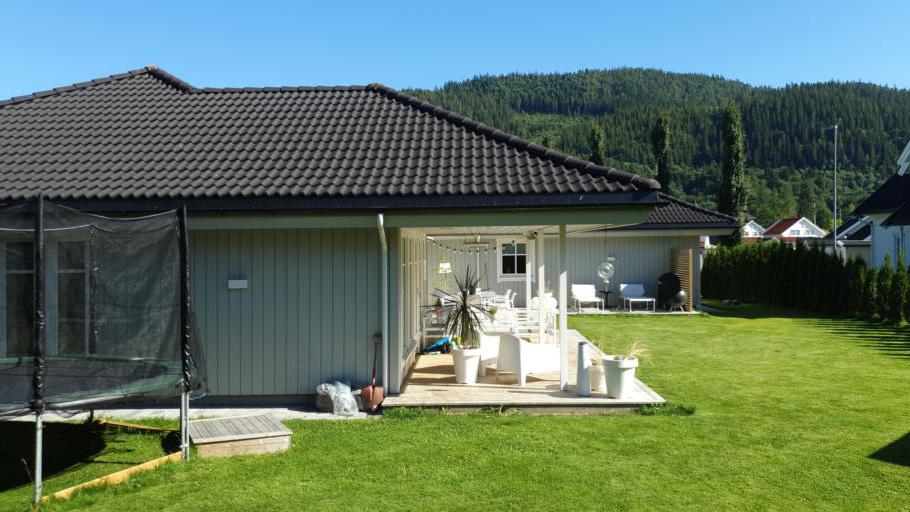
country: NO
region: Sor-Trondelag
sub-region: Orkdal
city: Orkanger
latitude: 63.2849
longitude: 9.8397
